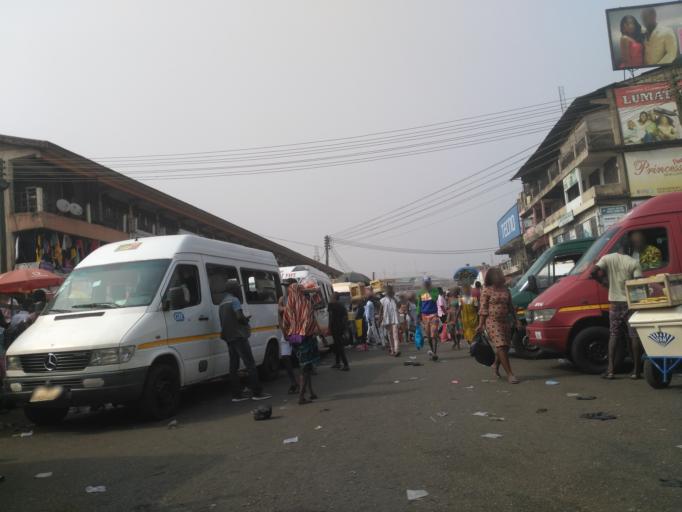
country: GH
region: Ashanti
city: Kumasi
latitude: 6.6955
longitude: -1.6203
